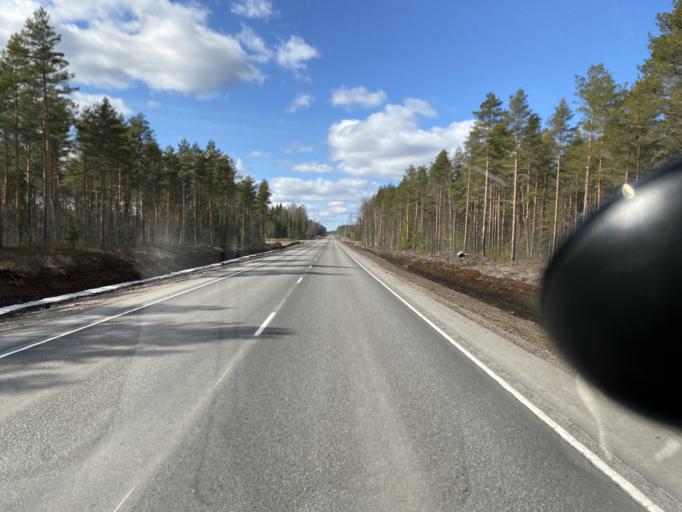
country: FI
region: Satakunta
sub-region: Pori
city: Huittinen
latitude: 61.1743
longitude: 22.5522
